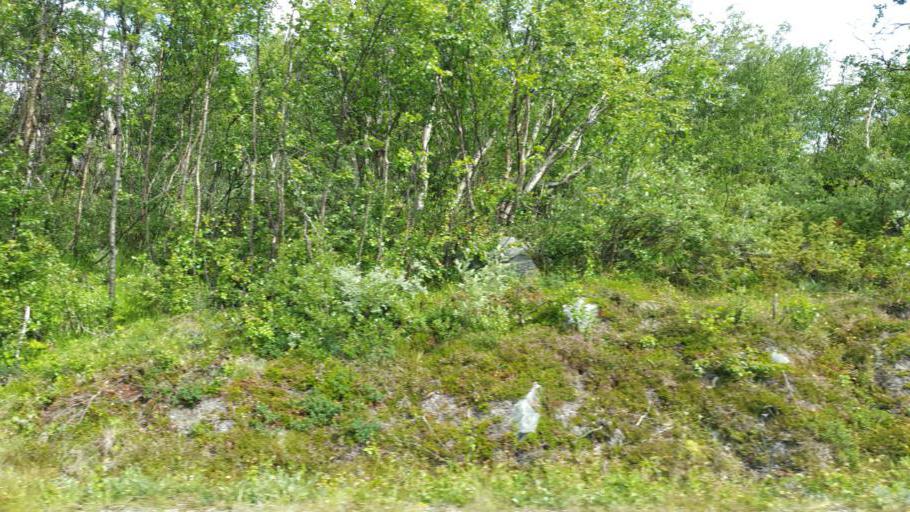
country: NO
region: Oppland
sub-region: Oystre Slidre
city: Heggenes
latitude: 61.4900
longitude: 8.8213
